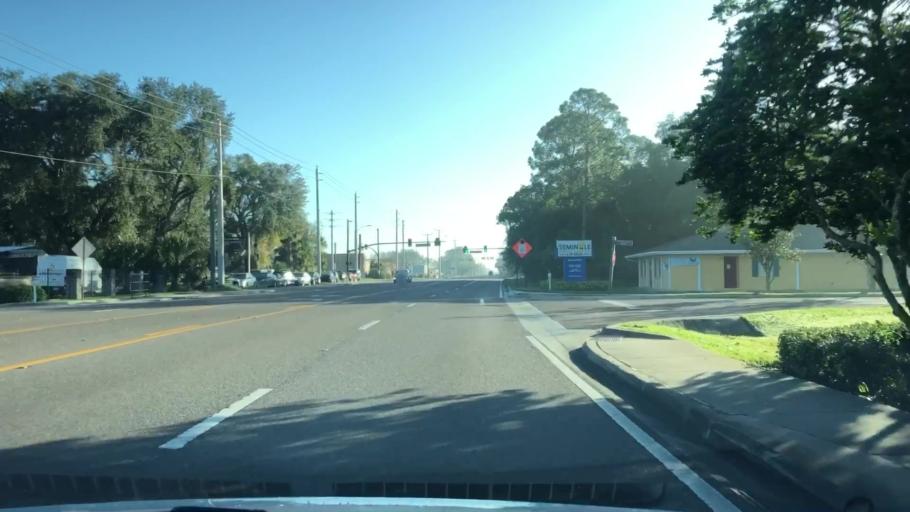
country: US
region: Florida
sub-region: Seminole County
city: Sanford
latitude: 28.7865
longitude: -81.2949
